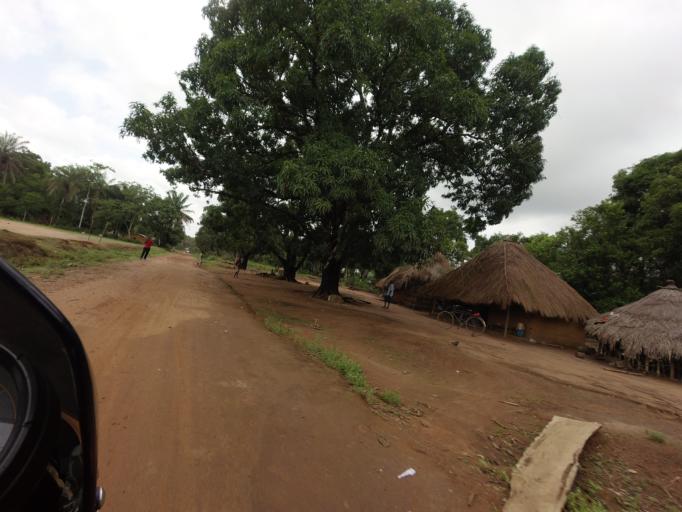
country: SL
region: Northern Province
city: Kassiri
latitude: 9.0279
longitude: -13.0653
